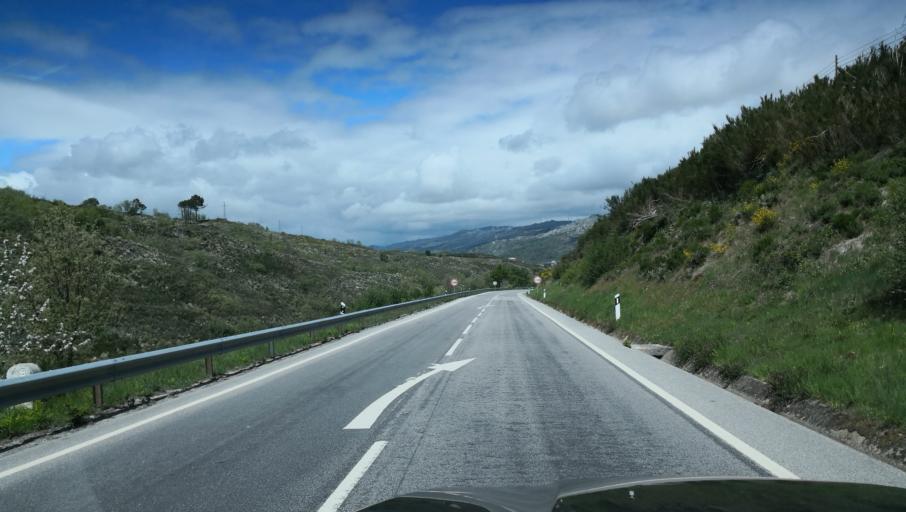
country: PT
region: Vila Real
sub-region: Vila Pouca de Aguiar
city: Vila Pouca de Aguiar
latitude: 41.4034
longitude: -7.6974
